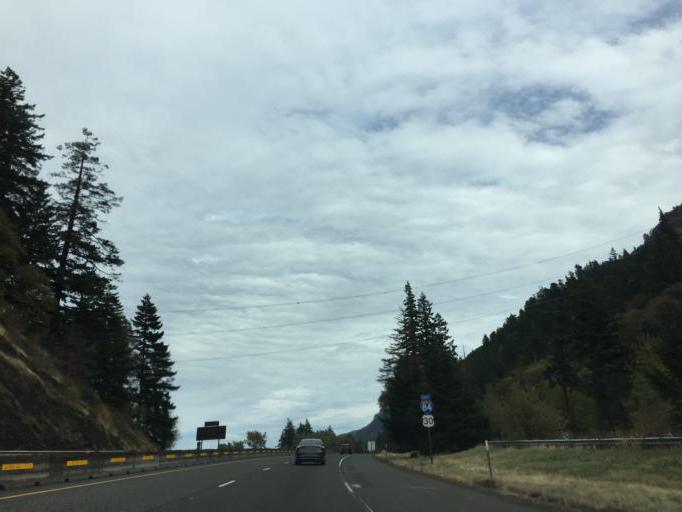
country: US
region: Oregon
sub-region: Hood River County
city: Cascade Locks
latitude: 45.6348
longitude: -121.9493
